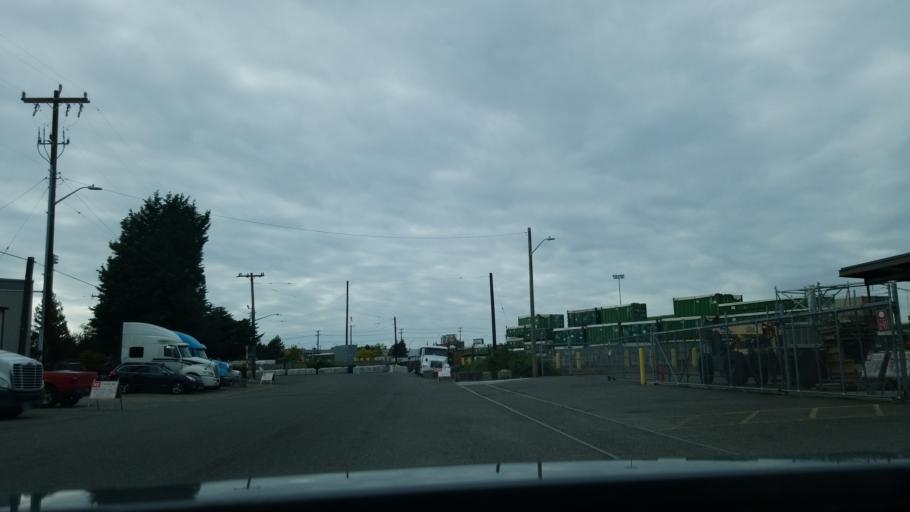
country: US
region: Washington
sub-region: King County
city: White Center
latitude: 47.5552
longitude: -122.3263
